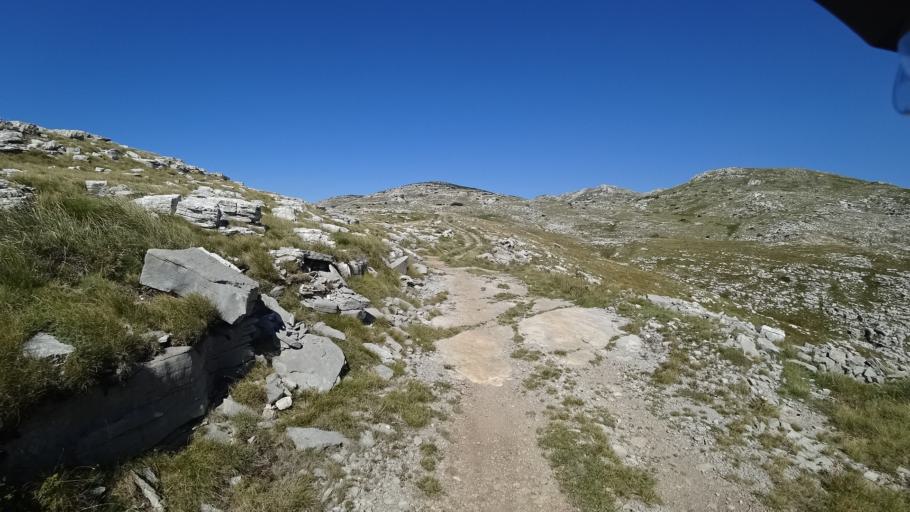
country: HR
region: Splitsko-Dalmatinska
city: Hrvace
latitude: 43.9259
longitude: 16.6045
